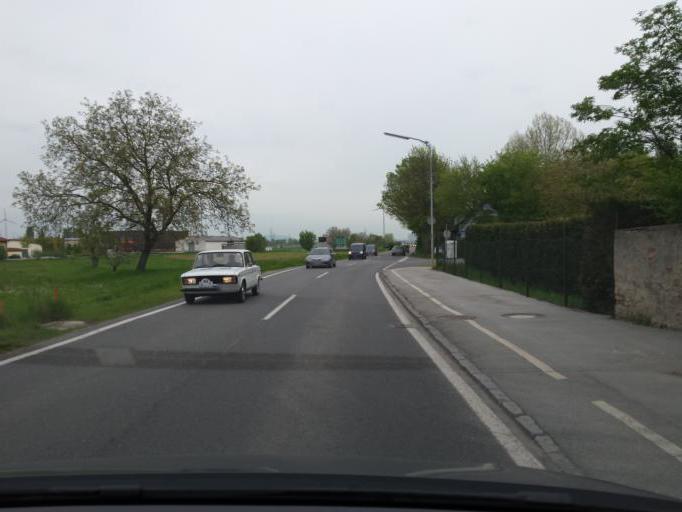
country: AT
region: Burgenland
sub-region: Politischer Bezirk Neusiedl am See
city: Bruckneudorf
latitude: 48.0286
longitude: 16.7880
